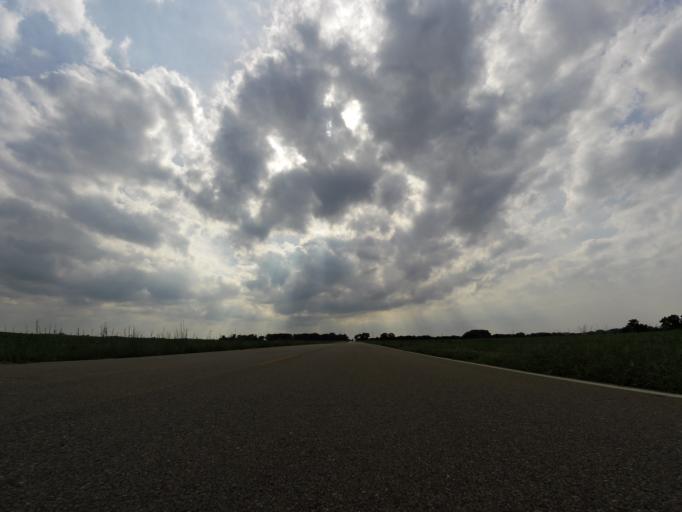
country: US
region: Kansas
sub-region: Reno County
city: South Hutchinson
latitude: 37.8977
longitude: -98.0555
